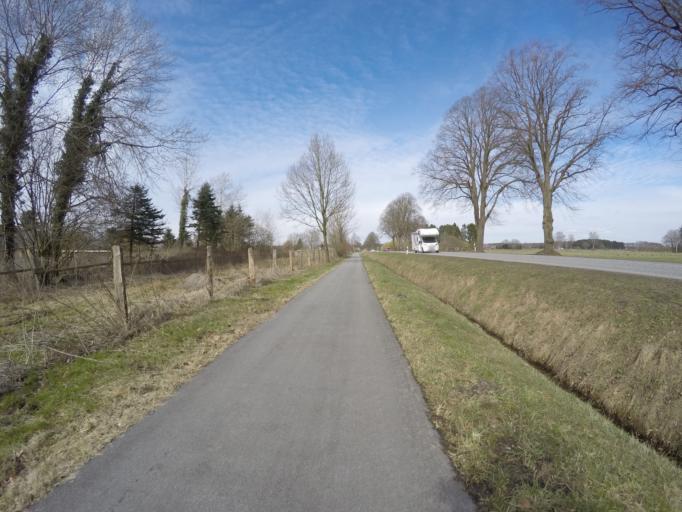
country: DE
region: Schleswig-Holstein
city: Langeln
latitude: 53.8054
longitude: 9.8787
